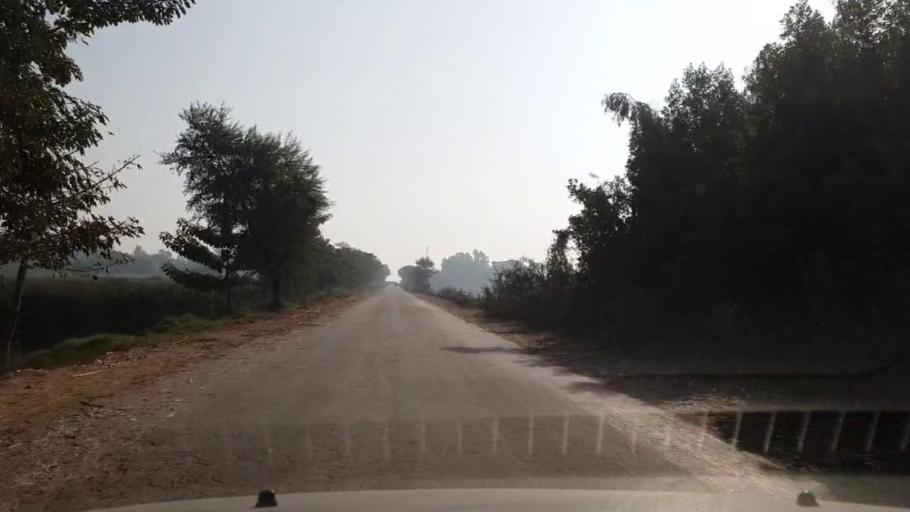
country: PK
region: Sindh
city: Matiari
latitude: 25.5816
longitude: 68.4941
